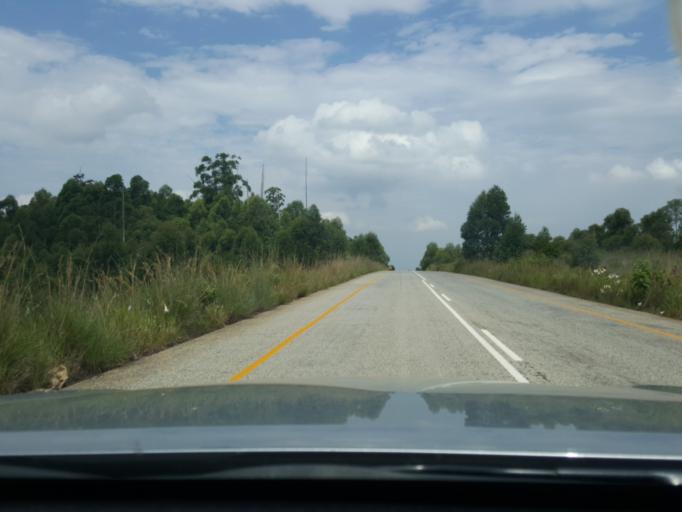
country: ZA
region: Mpumalanga
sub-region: Ehlanzeni District
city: White River
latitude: -25.1923
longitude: 30.9092
